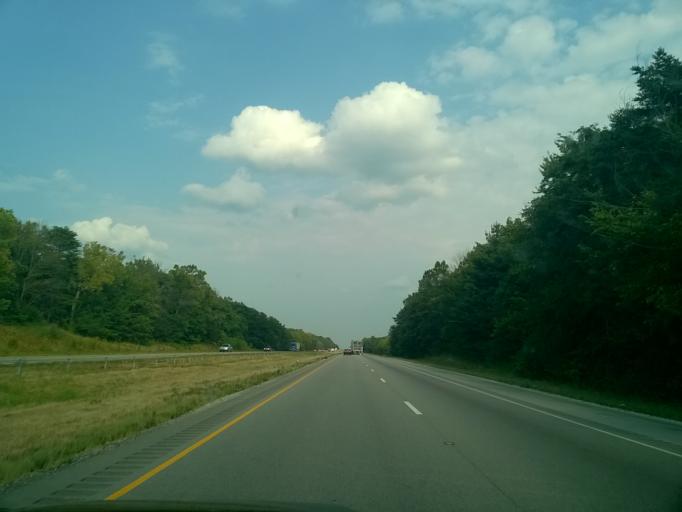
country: US
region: Indiana
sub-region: Vigo County
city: Seelyville
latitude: 39.4510
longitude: -87.1910
